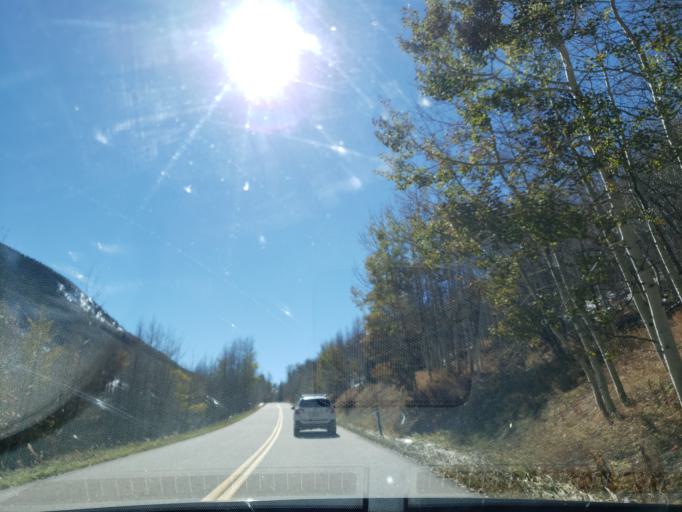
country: US
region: Colorado
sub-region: Pitkin County
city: Snowmass Village
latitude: 39.1189
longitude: -106.9100
